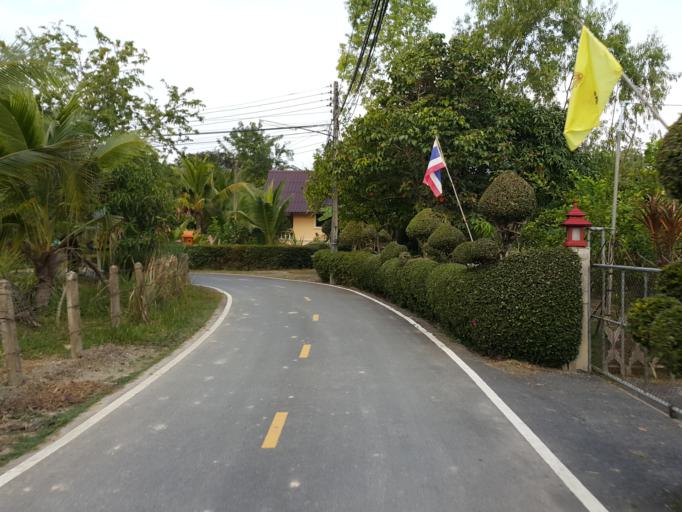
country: TH
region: Chiang Mai
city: San Sai
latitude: 18.8198
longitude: 99.0785
